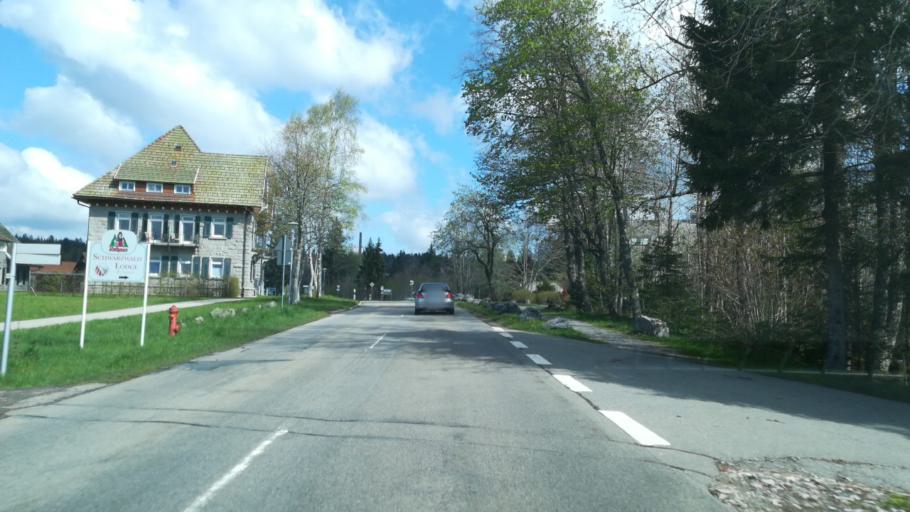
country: DE
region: Baden-Wuerttemberg
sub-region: Freiburg Region
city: Grafenhausen
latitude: 47.7915
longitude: 8.2469
